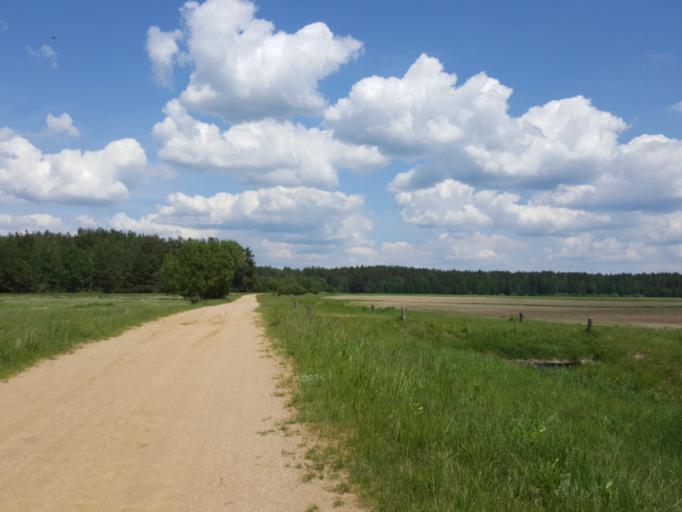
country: BY
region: Brest
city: Kamyanyuki
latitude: 52.5389
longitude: 23.7047
